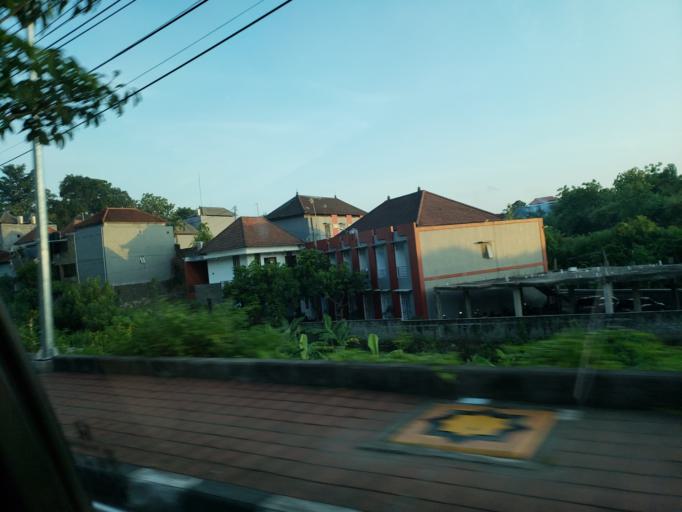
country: ID
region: Bali
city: Jimbaran
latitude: -8.7999
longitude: 115.1673
